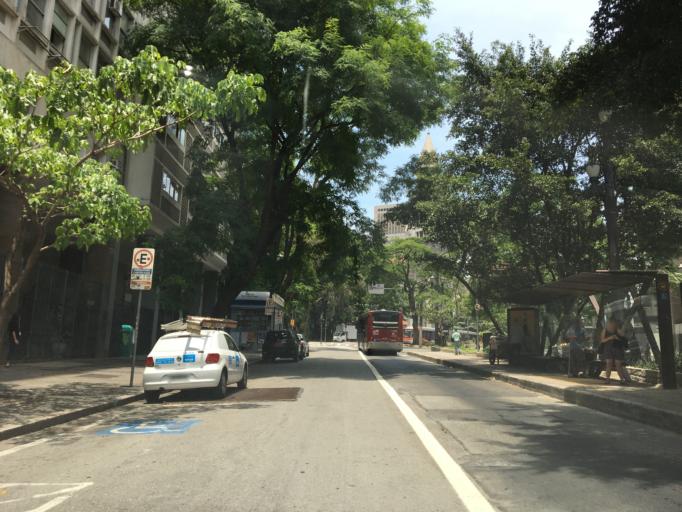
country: BR
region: Sao Paulo
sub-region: Sao Paulo
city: Sao Paulo
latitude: -23.5467
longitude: -46.6454
